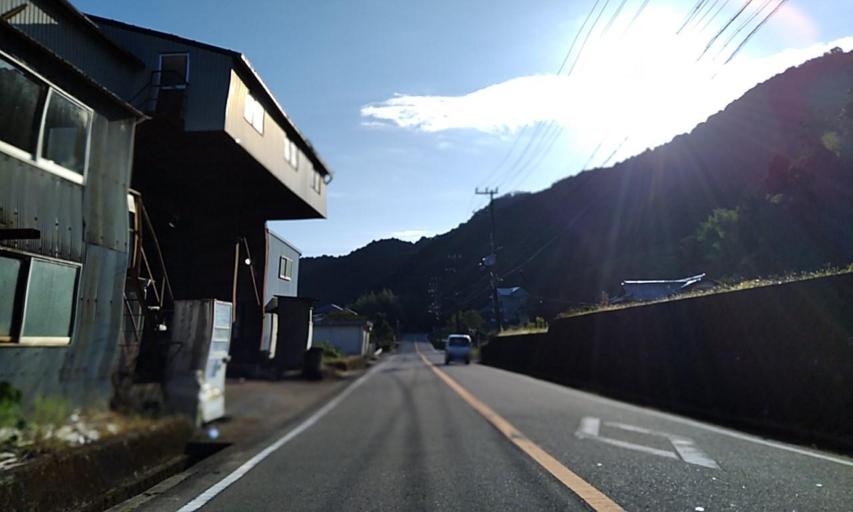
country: JP
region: Wakayama
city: Iwade
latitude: 34.1522
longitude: 135.3126
